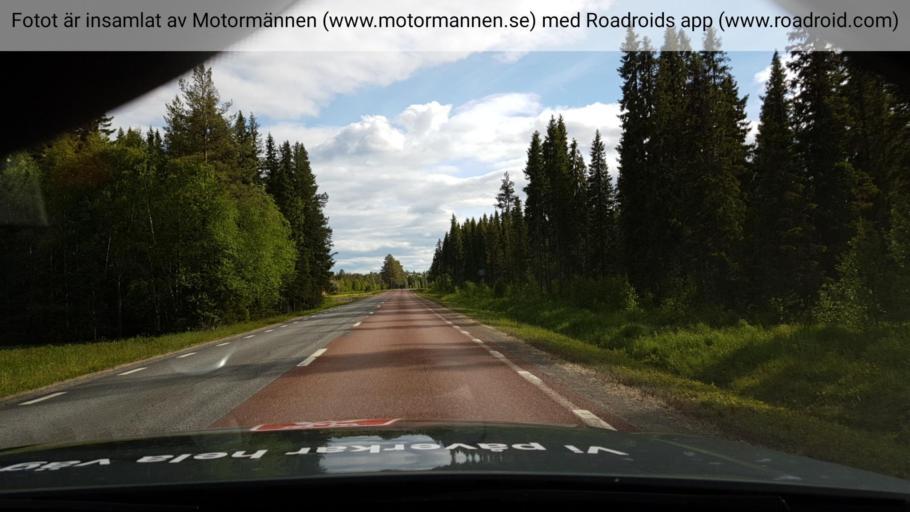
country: SE
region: Jaemtland
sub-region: Stroemsunds Kommun
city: Stroemsund
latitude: 63.7513
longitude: 15.4967
